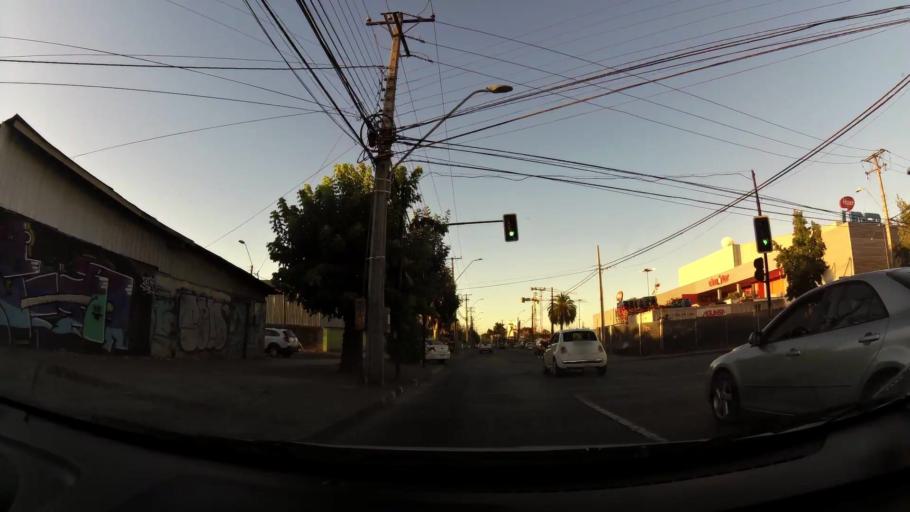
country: CL
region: Maule
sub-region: Provincia de Curico
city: Curico
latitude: -34.9786
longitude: -71.2397
